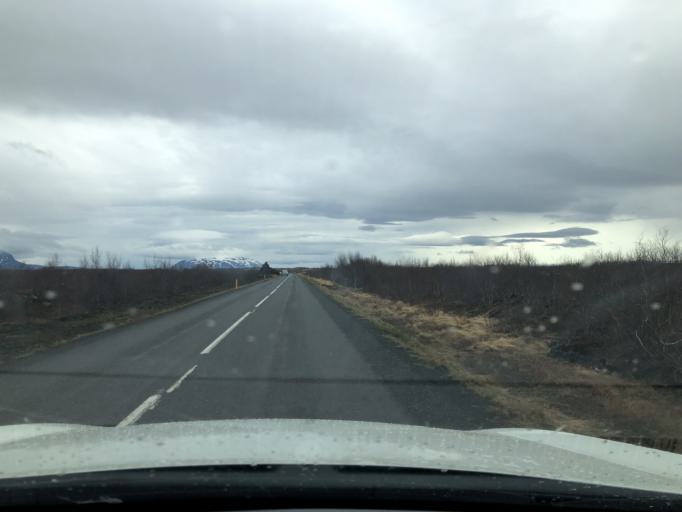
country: IS
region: Northeast
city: Laugar
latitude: 65.6064
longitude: -16.9214
